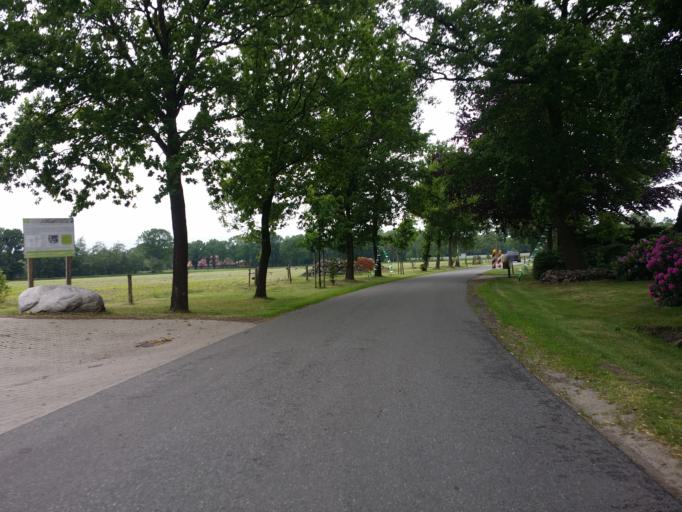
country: DE
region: Lower Saxony
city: Hatten
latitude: 53.0930
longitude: 8.3775
